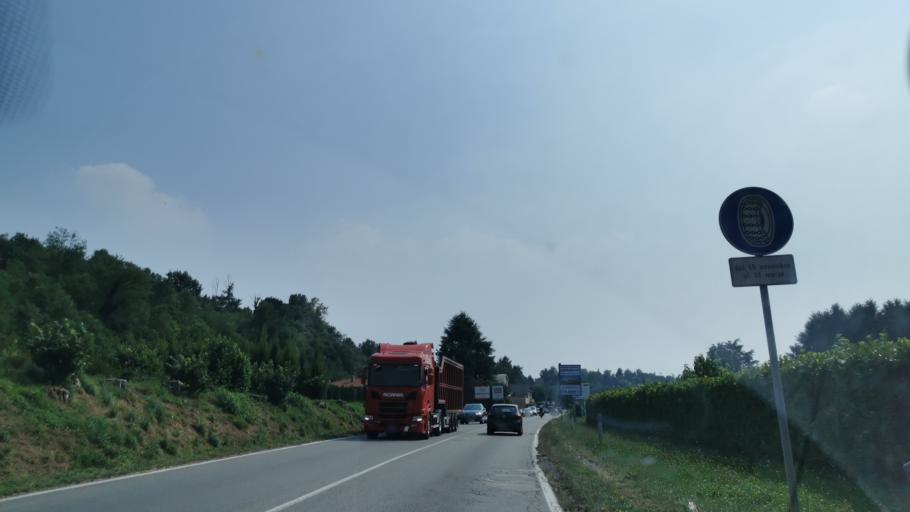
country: IT
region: Lombardy
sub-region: Provincia di Lecco
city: Canova-San Zeno
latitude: 45.7155
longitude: 9.4077
